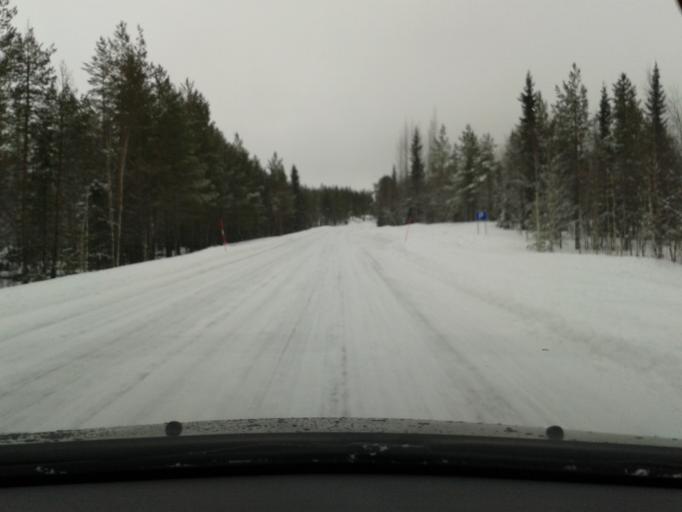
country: SE
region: Vaesterbotten
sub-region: Vilhelmina Kommun
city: Sjoberg
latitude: 64.8706
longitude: 15.8897
